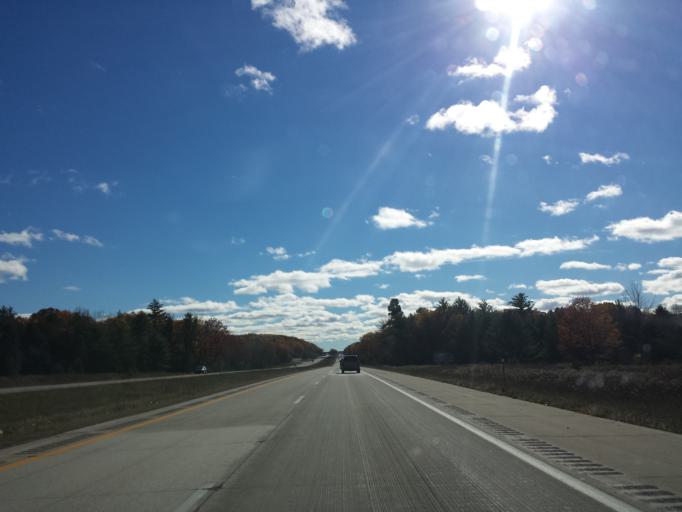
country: US
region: Michigan
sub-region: Cheboygan County
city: Indian River
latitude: 45.5114
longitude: -84.6160
